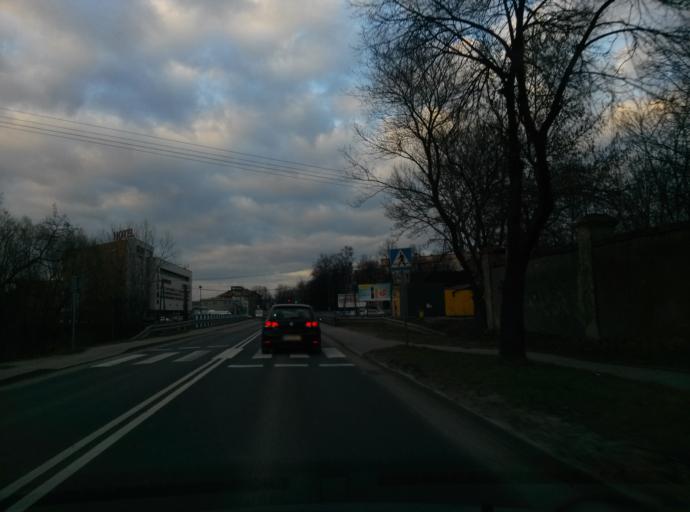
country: PL
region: Lesser Poland Voivodeship
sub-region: Powiat brzeski
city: Brzesko
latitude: 49.9615
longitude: 20.5976
